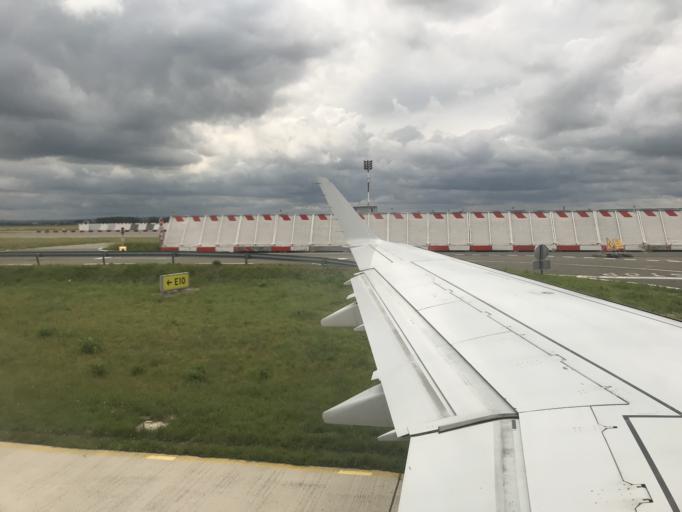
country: FR
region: Ile-de-France
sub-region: Departement de Seine-et-Marne
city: Mitry-Mory
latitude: 49.0029
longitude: 2.5984
